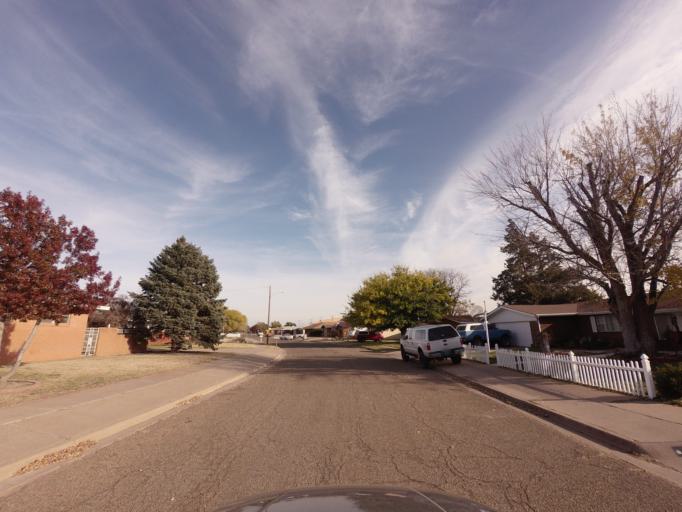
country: US
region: New Mexico
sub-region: Curry County
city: Clovis
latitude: 34.4215
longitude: -103.2168
